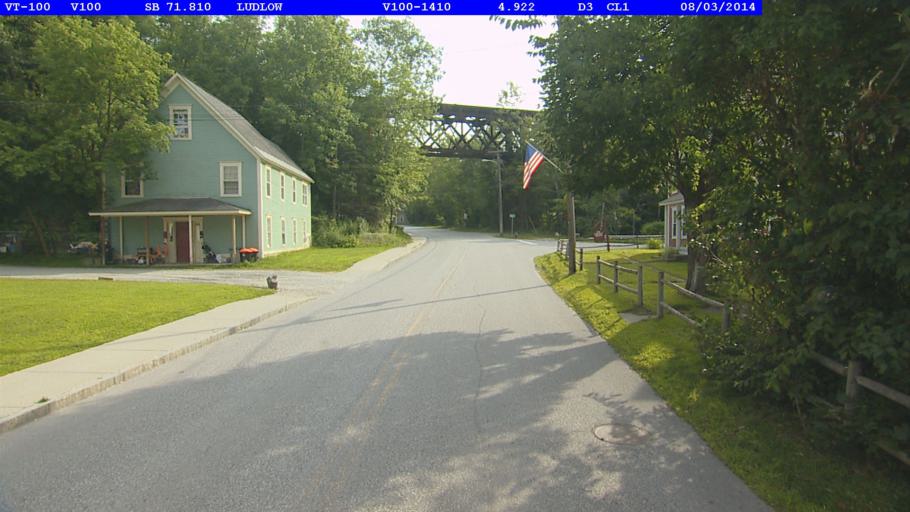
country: US
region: Vermont
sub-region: Windsor County
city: Chester
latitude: 43.3945
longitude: -72.7037
